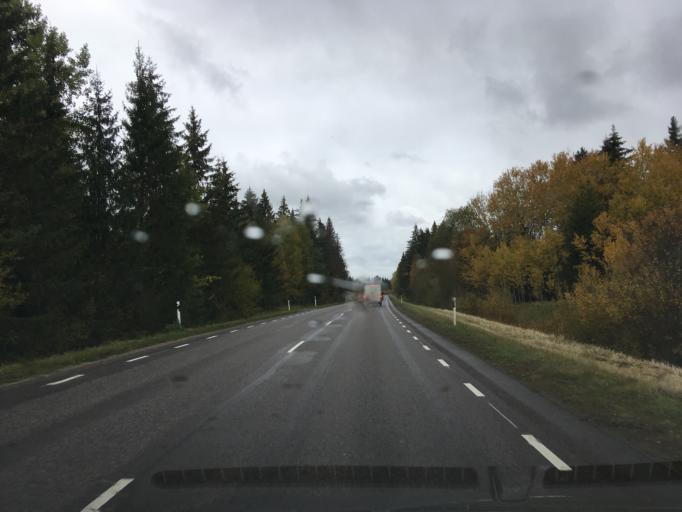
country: EE
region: Harju
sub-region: Anija vald
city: Kehra
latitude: 59.3342
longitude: 25.3125
